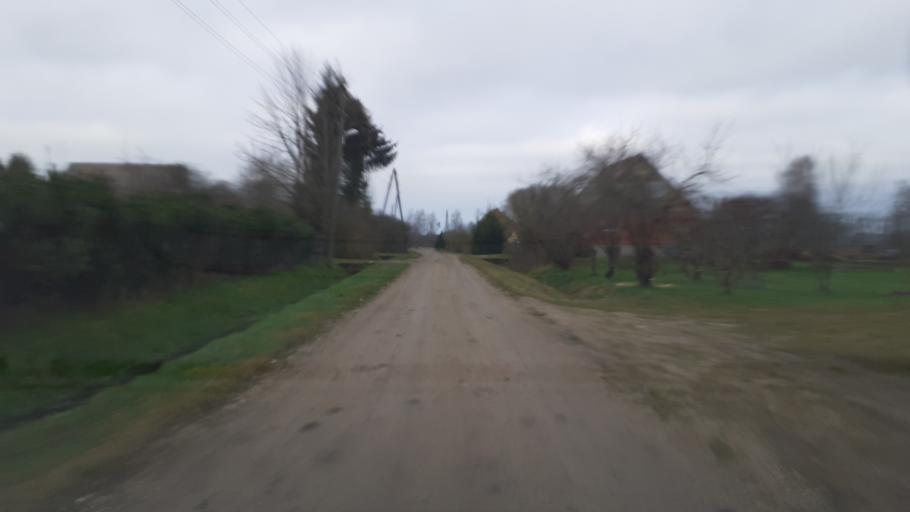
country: LV
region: Aizpute
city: Aizpute
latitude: 56.8021
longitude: 21.6696
